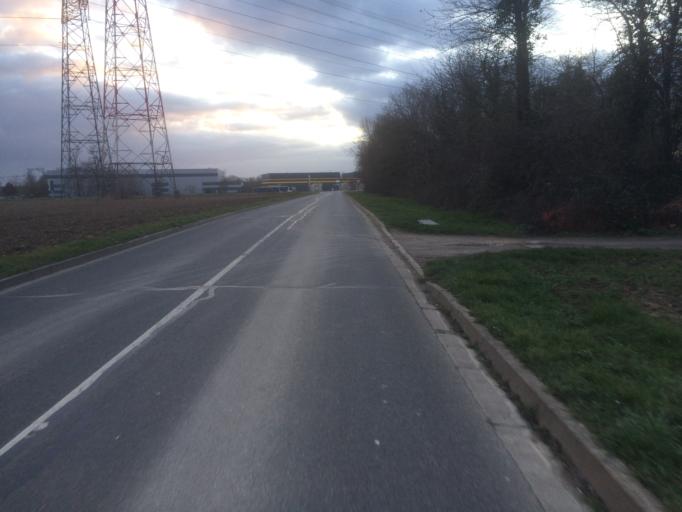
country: FR
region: Ile-de-France
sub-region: Departement de l'Essonne
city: Villejust
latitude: 48.6677
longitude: 2.2098
